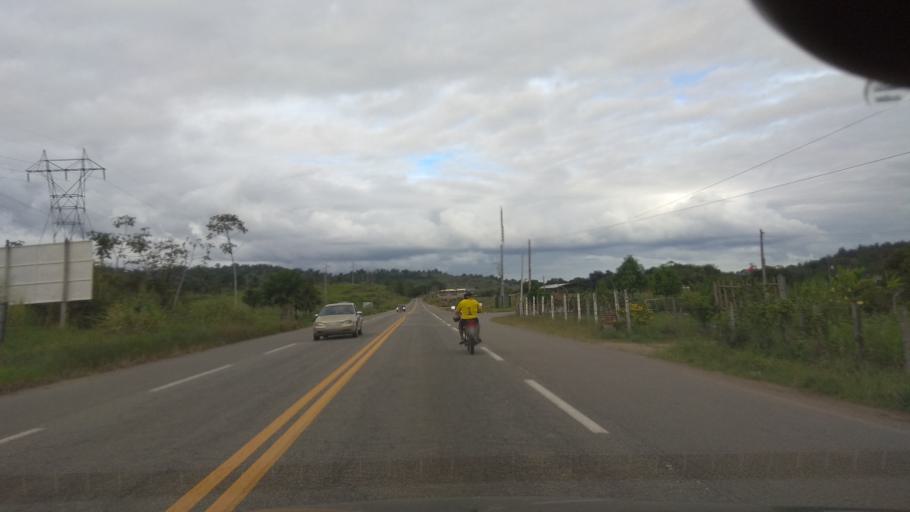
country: BR
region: Bahia
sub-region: Ipiau
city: Ipiau
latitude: -14.1745
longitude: -39.6788
